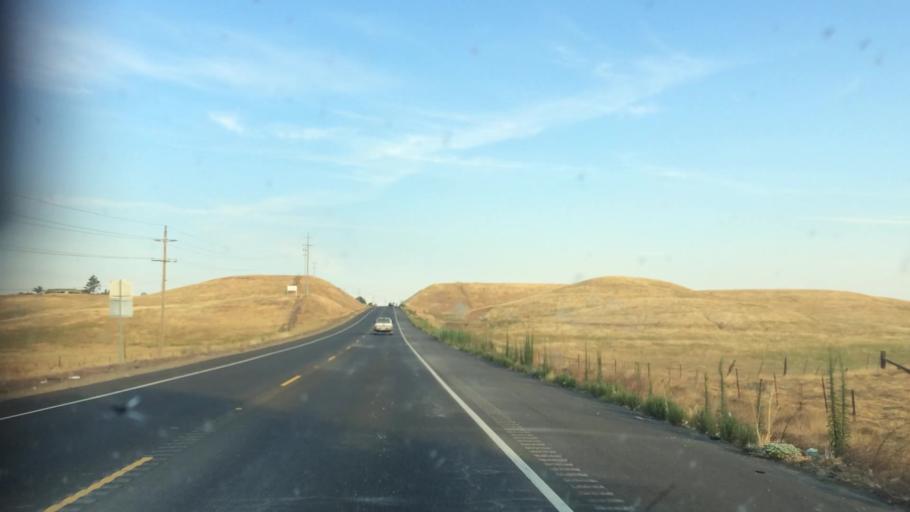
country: US
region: California
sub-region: Sacramento County
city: Rancho Murieta
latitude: 38.4973
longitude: -121.1989
